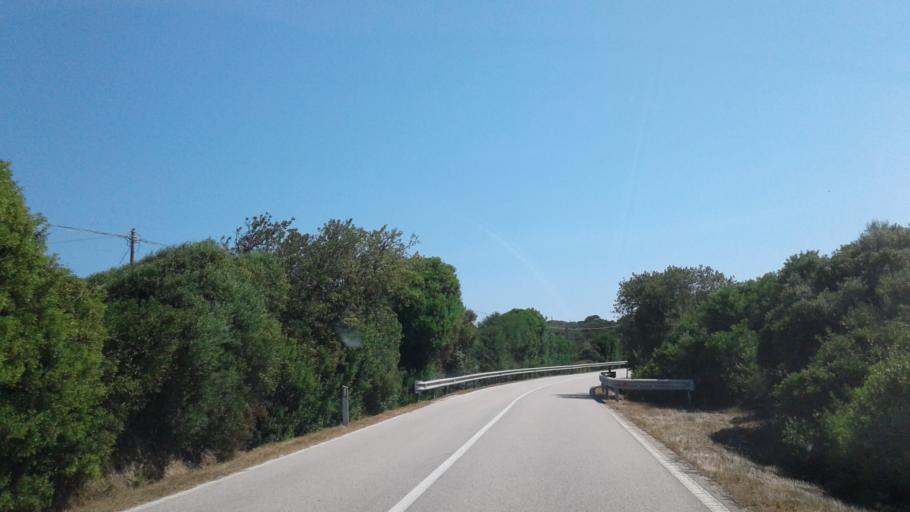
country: IT
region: Sardinia
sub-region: Provincia di Olbia-Tempio
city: Luogosanto
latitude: 41.1261
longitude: 9.2775
